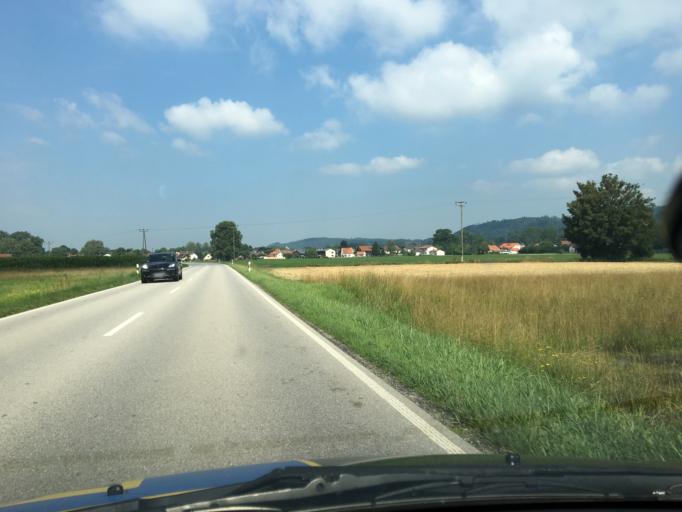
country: DE
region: Bavaria
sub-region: Upper Bavaria
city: Neuotting
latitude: 48.2527
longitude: 12.6793
